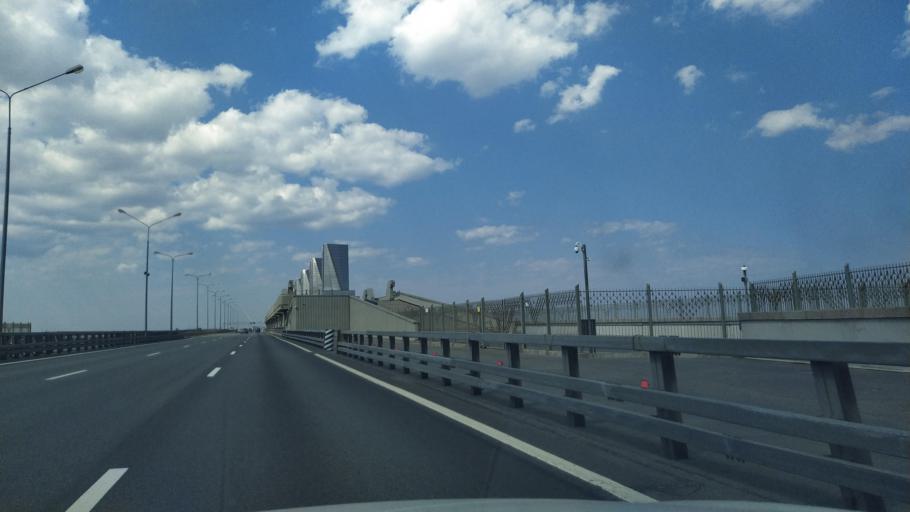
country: RU
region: Leningrad
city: Gorskaya
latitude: 60.0337
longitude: 29.9122
